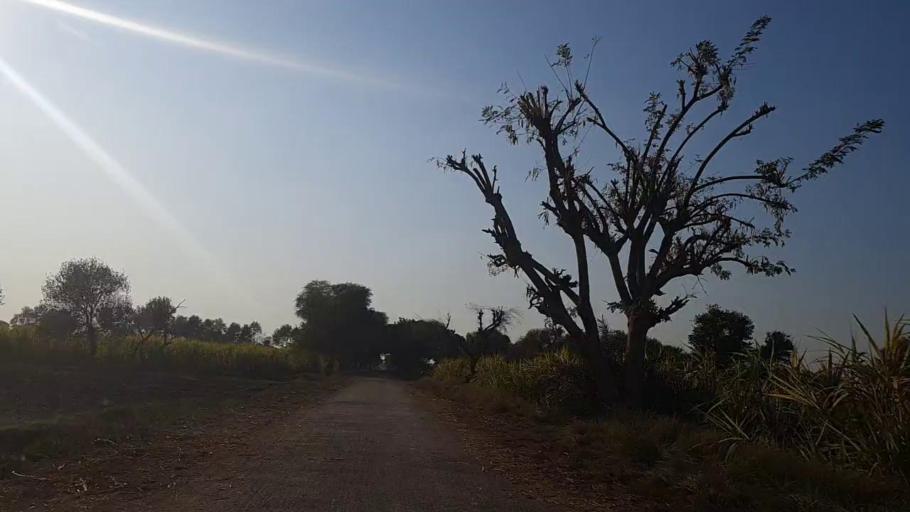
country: PK
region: Sindh
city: Daur
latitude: 26.3331
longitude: 68.1612
